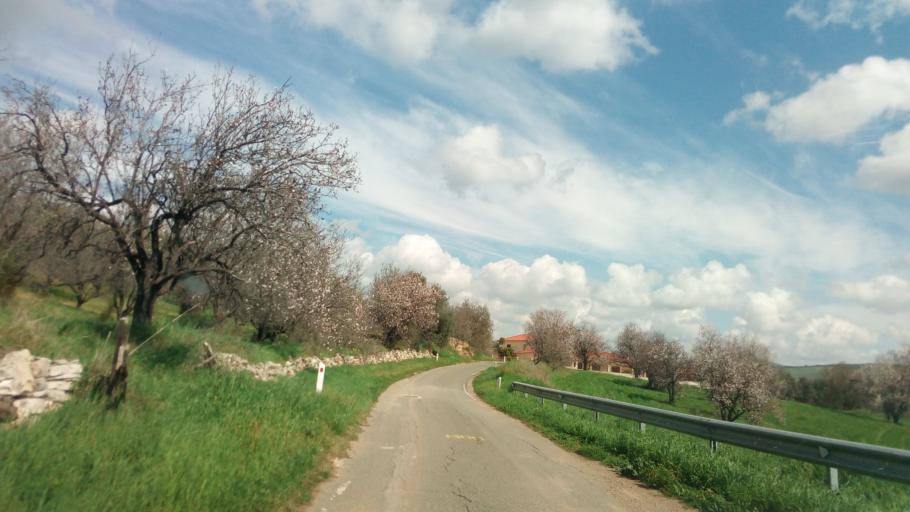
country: CY
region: Pafos
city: Mesogi
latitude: 34.7727
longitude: 32.5690
